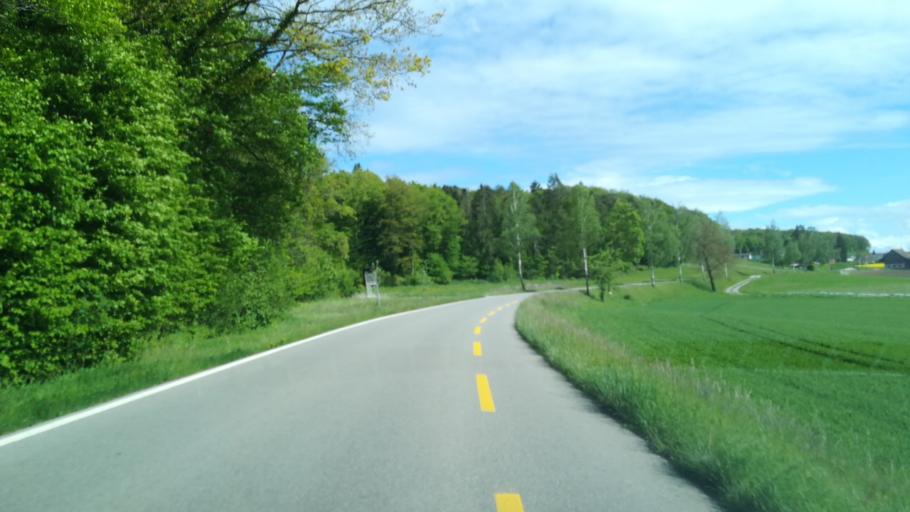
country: CH
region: Schaffhausen
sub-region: Bezirk Reiat
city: Thayngen
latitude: 47.7182
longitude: 8.7206
